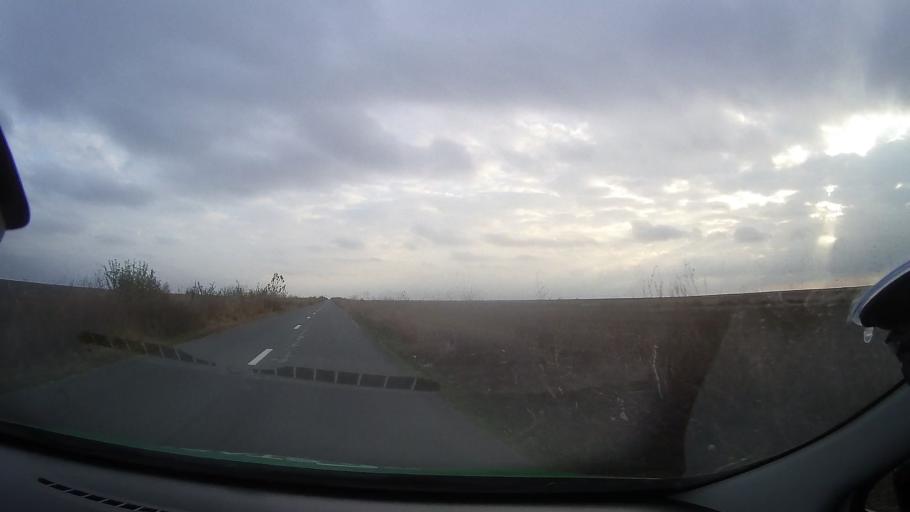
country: RO
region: Constanta
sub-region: Comuna Pestera
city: Pestera
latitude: 44.1460
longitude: 28.1154
